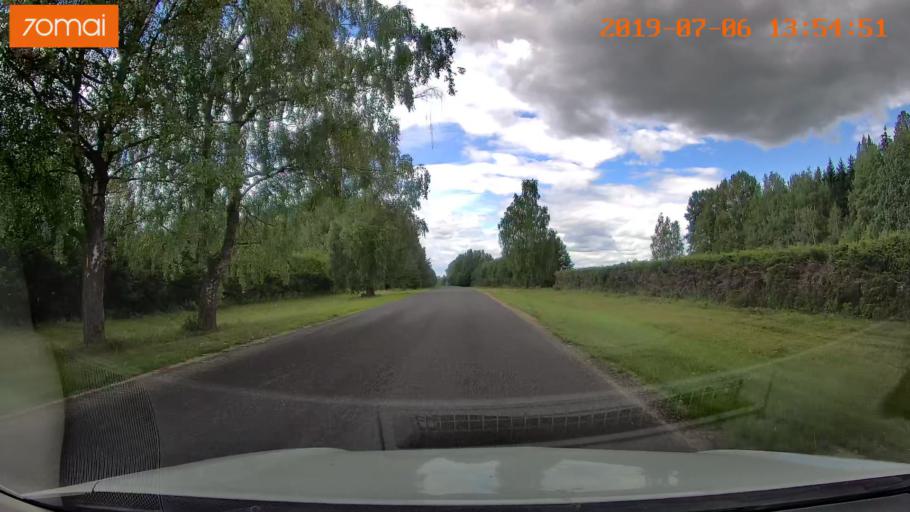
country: BY
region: Minsk
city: Ivyanyets
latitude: 53.7499
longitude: 26.8157
